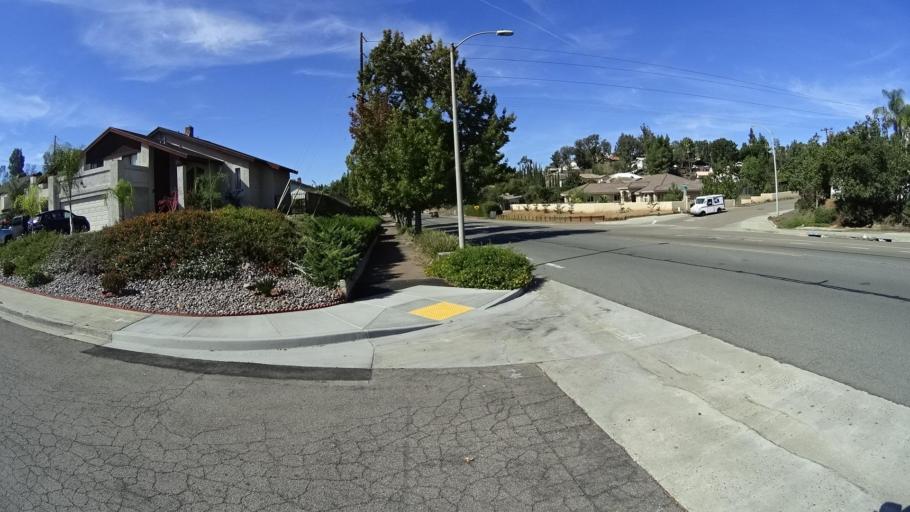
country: US
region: California
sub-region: San Diego County
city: Rancho San Diego
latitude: 32.7512
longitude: -116.9531
